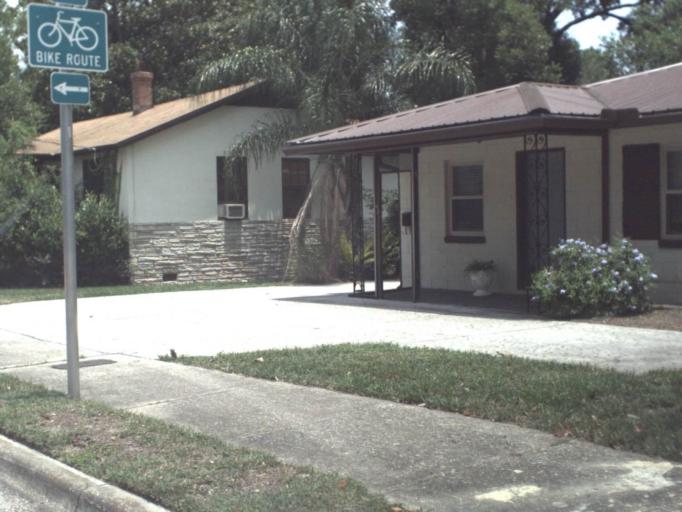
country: US
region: Florida
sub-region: Duval County
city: Jacksonville
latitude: 30.2914
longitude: -81.7241
